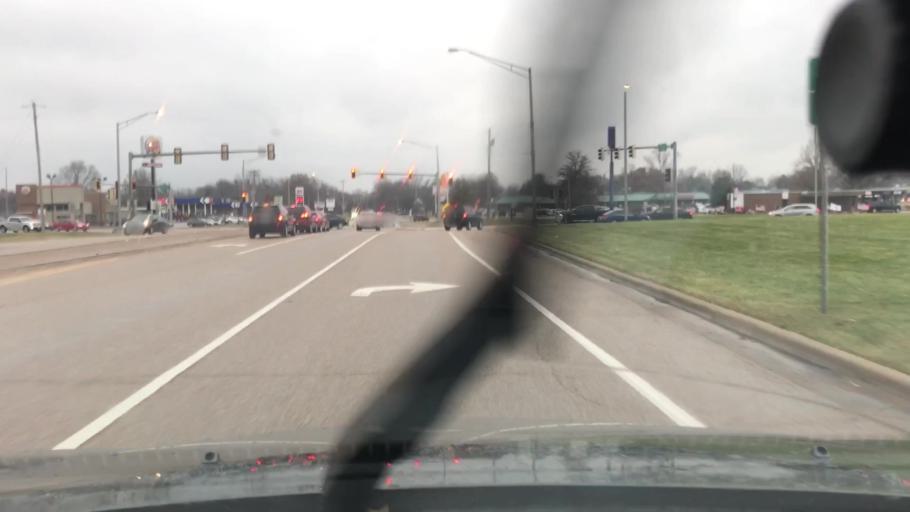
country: US
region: Illinois
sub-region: Madison County
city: Bethalto
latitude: 38.9002
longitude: -90.0593
